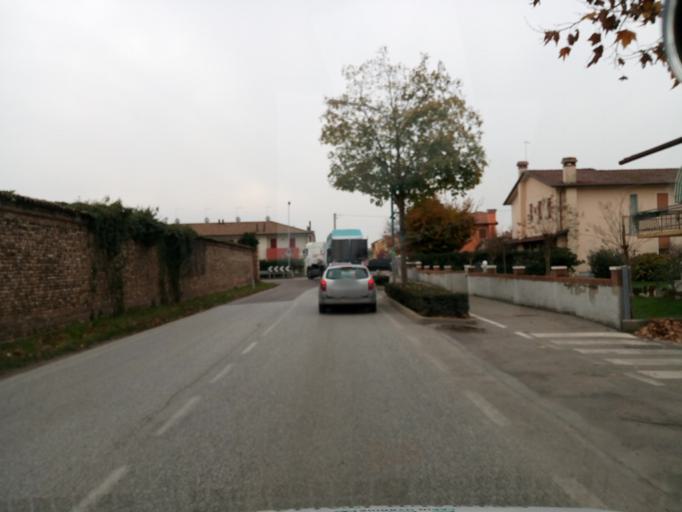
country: IT
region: Veneto
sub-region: Provincia di Treviso
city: Fanzolo
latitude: 45.7194
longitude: 12.0134
